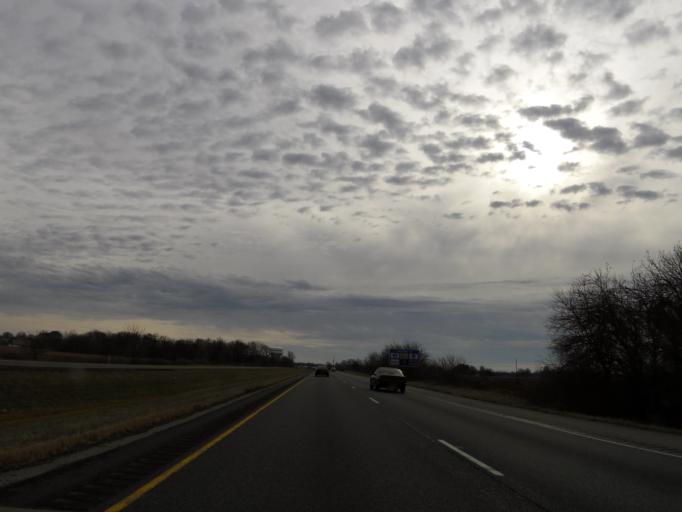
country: US
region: Indiana
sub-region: Hendricks County
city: Brownsburg
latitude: 39.8698
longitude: -86.4212
